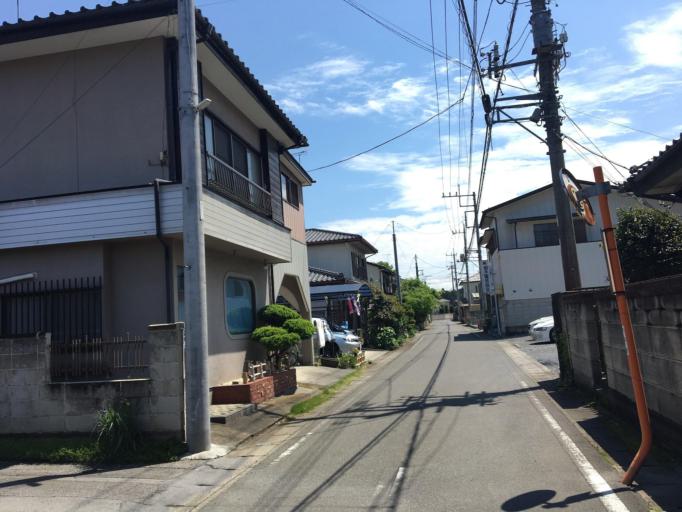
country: JP
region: Tochigi
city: Tochigi
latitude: 36.3406
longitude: 139.6984
